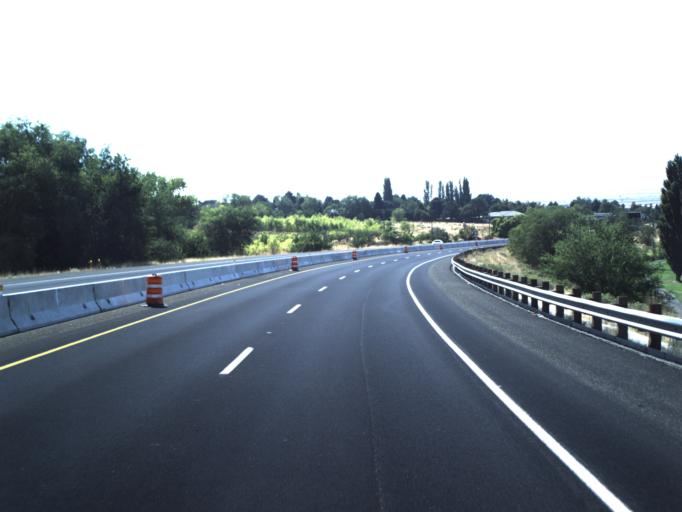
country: US
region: Utah
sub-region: Box Elder County
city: Brigham City
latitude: 41.4872
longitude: -112.0059
